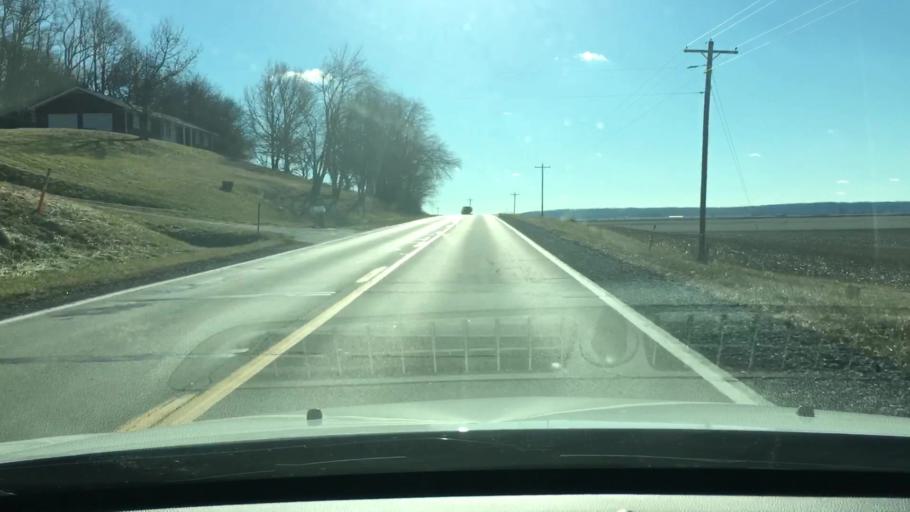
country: US
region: Illinois
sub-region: Morgan County
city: Meredosia
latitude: 39.6996
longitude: -90.5708
